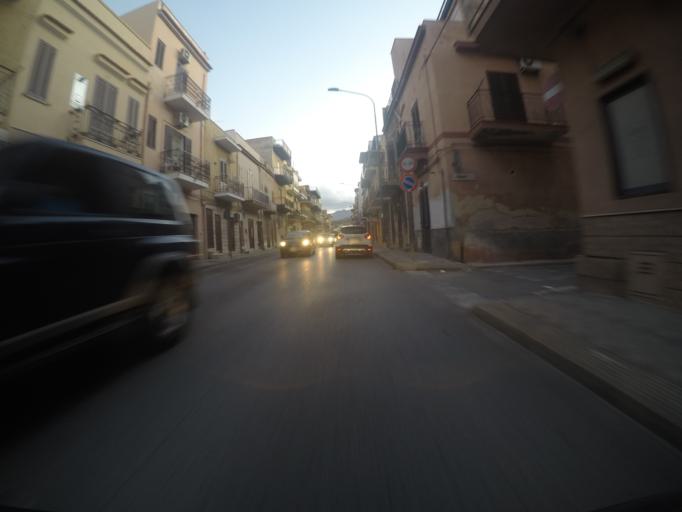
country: IT
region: Sicily
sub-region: Palermo
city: Capaci
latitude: 38.1745
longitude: 13.2414
